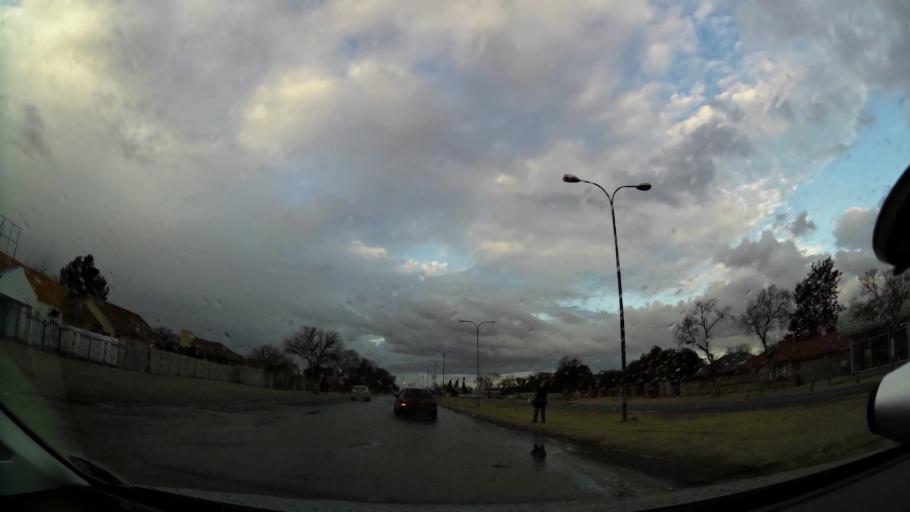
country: ZA
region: Orange Free State
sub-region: Lejweleputswa District Municipality
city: Welkom
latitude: -27.9747
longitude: 26.7635
